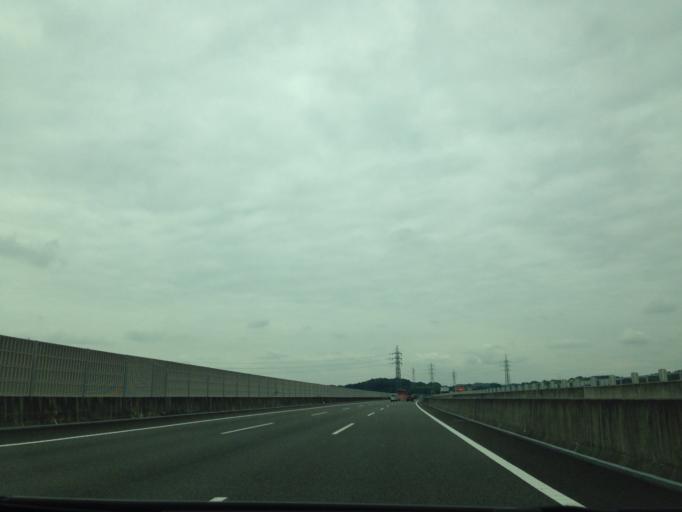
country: JP
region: Shizuoka
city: Mori
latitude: 34.8225
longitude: 137.9238
